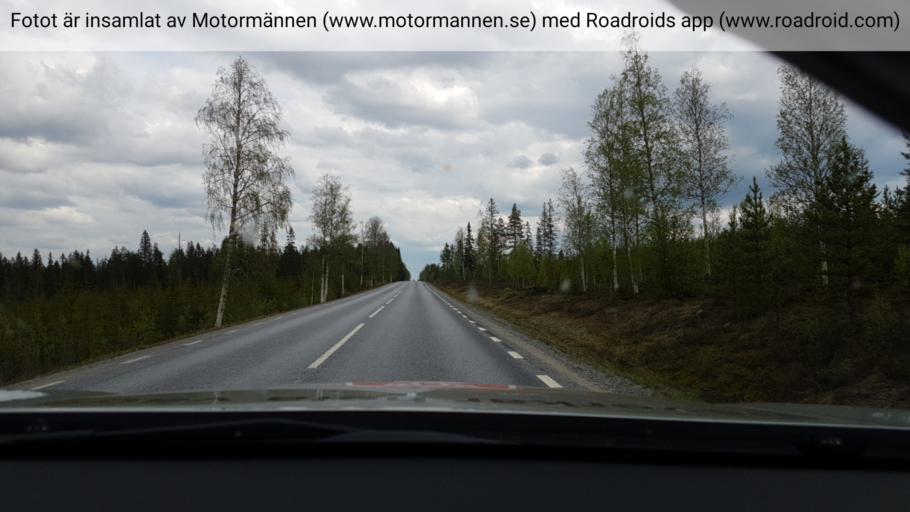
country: SE
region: Vaesterbotten
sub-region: Bjurholms Kommun
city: Bjurholm
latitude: 63.9599
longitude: 18.8602
